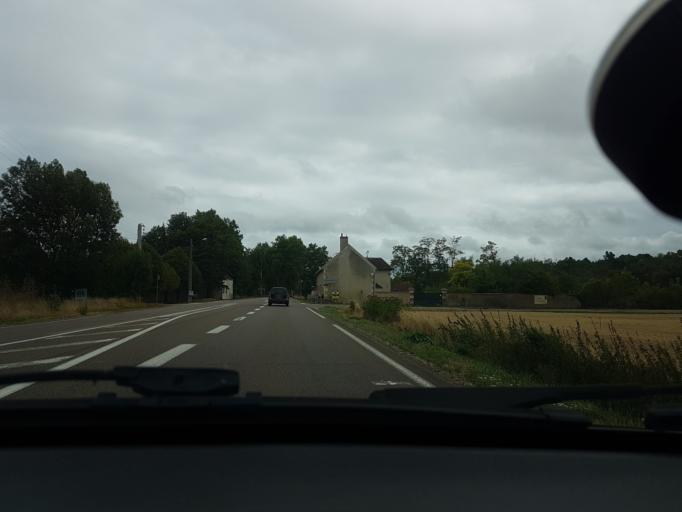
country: FR
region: Bourgogne
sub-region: Departement de l'Yonne
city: Champs-sur-Yonne
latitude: 47.7208
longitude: 3.6112
